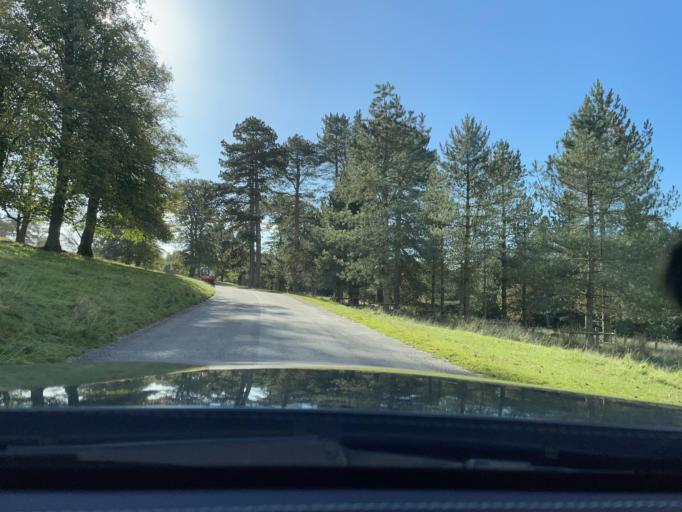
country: GB
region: England
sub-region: Cheshire East
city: Disley
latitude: 53.3417
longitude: -2.0564
